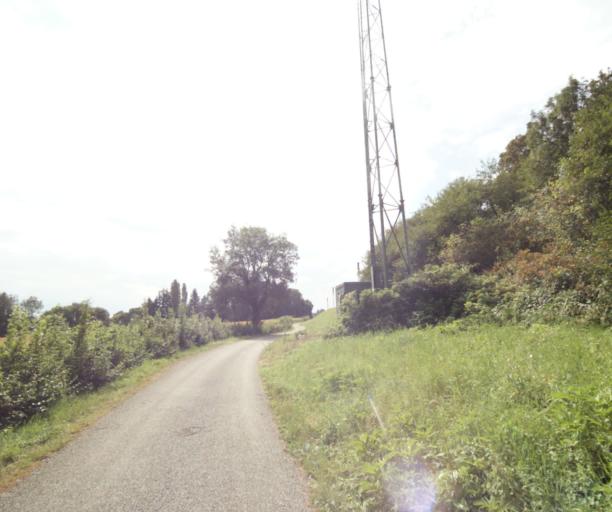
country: FR
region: Bourgogne
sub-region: Departement de Saone-et-Loire
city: Tournus
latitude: 46.5460
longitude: 4.9220
